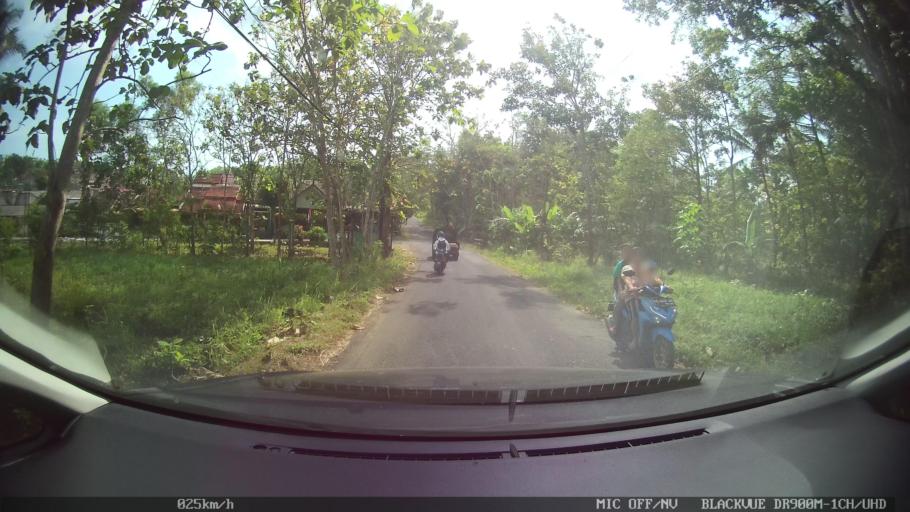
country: ID
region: Daerah Istimewa Yogyakarta
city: Bantul
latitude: -7.8593
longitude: 110.3041
